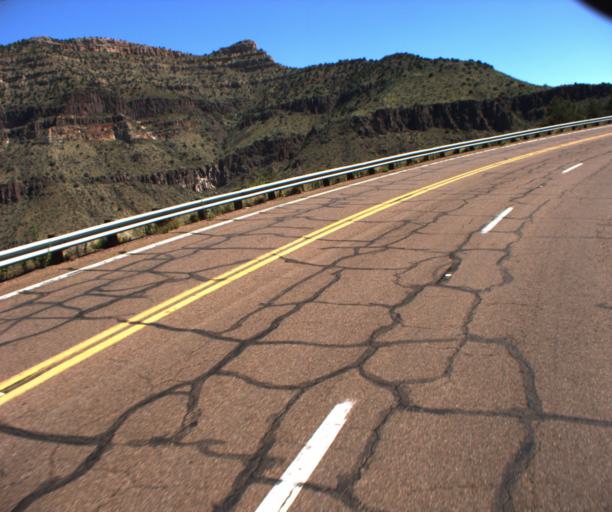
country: US
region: Arizona
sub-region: Navajo County
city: Cibecue
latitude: 33.7942
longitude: -110.4992
